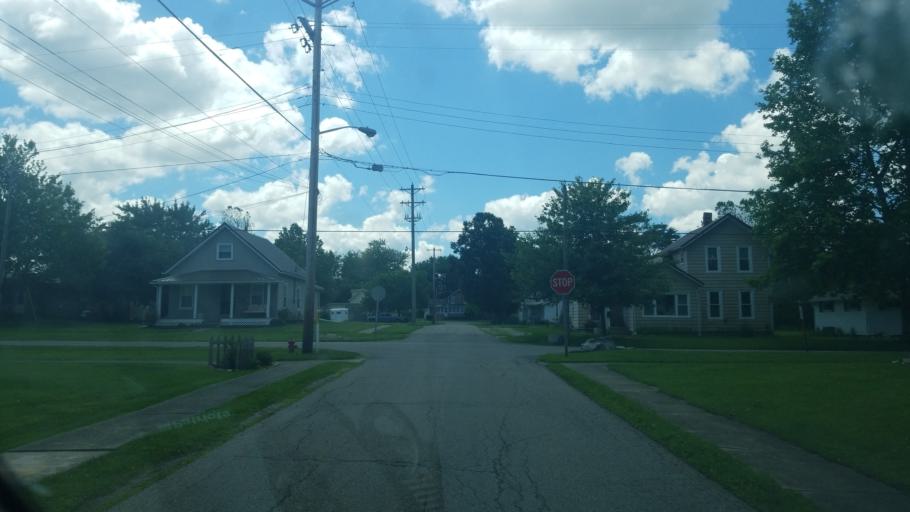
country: US
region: Ohio
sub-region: Huron County
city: New London
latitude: 41.0833
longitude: -82.3917
